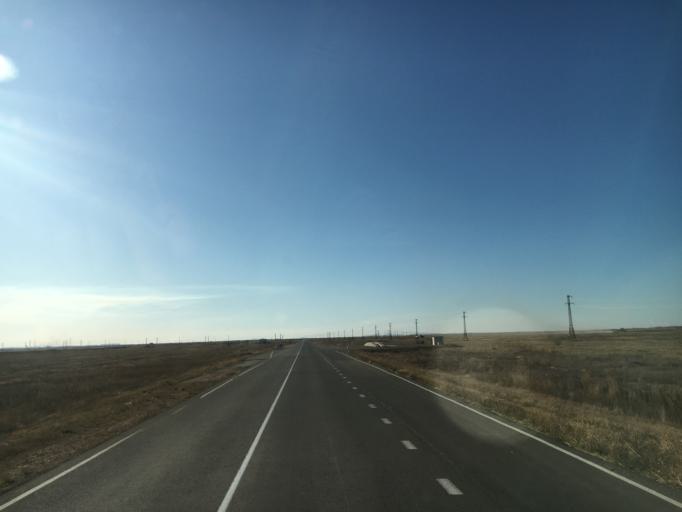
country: KZ
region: Qaraghandy
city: Tokarevka
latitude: 50.0993
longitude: 73.3124
